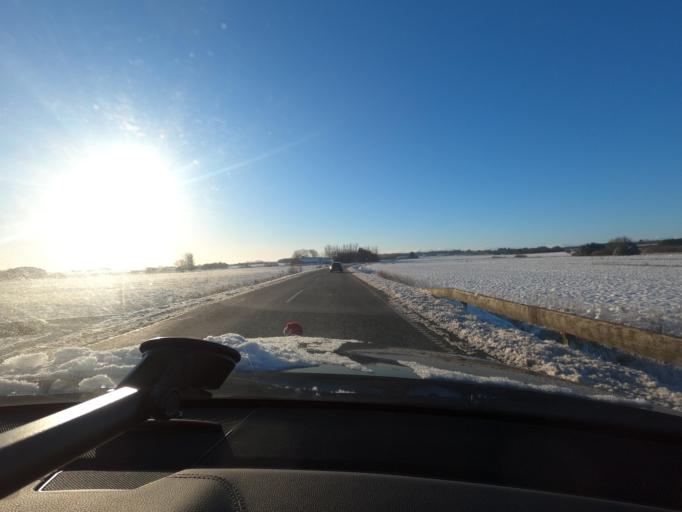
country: DK
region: South Denmark
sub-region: Tonder Kommune
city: Toftlund
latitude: 55.1718
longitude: 8.9884
